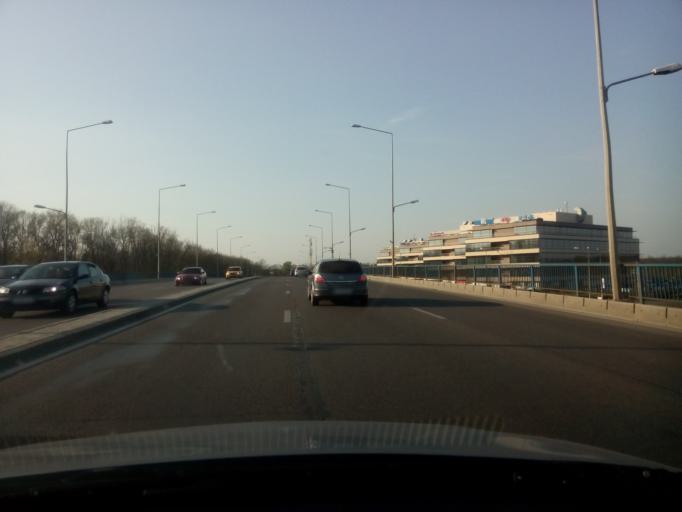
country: RO
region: Ilfov
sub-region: Comuna Otopeni
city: Otopeni
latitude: 44.5129
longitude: 26.0808
